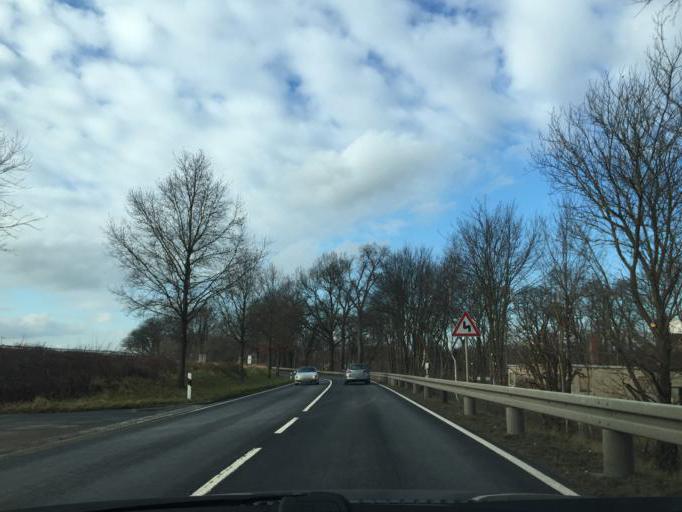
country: DE
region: Saxony
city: Radeburg
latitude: 51.2071
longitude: 13.7593
